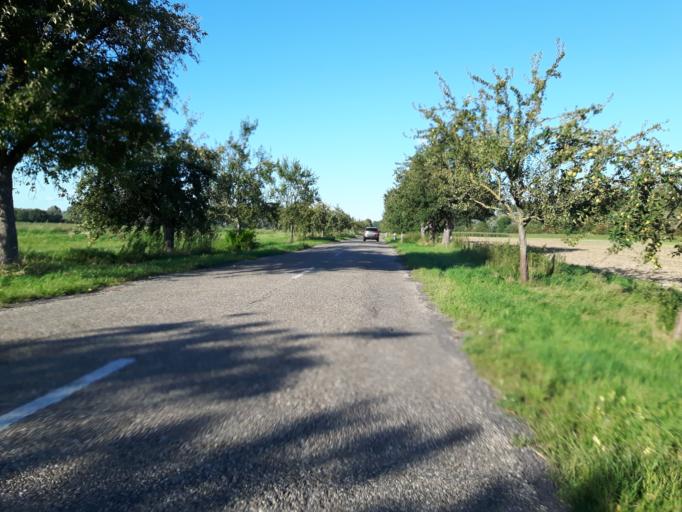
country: DE
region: Rheinland-Pfalz
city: Otterstadt
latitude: 49.3831
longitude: 8.4836
